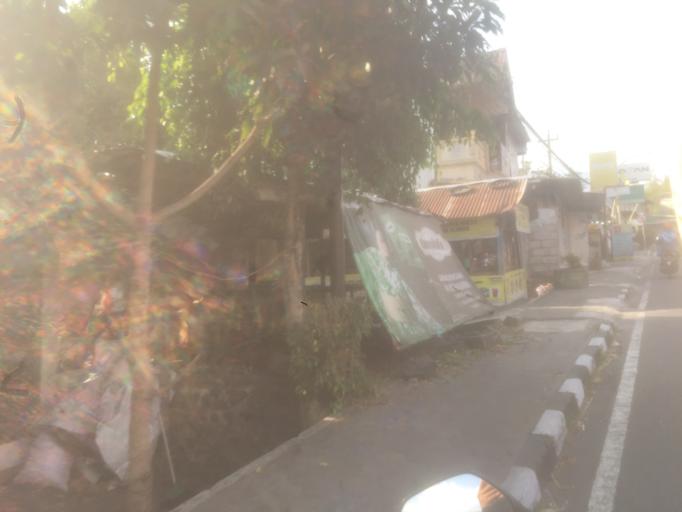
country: ID
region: Daerah Istimewa Yogyakarta
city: Sleman
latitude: -7.6663
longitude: 110.4190
